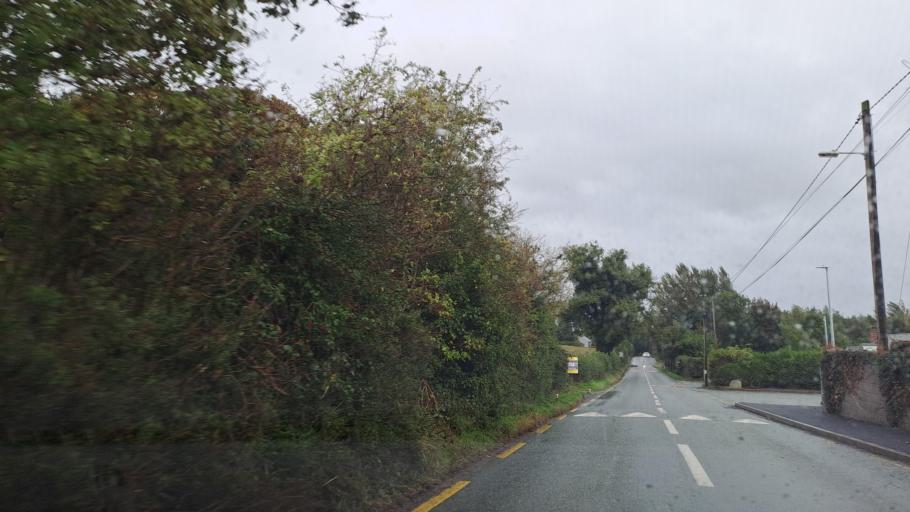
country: IE
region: Leinster
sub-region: Lu
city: Dundalk
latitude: 53.9677
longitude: -6.4771
